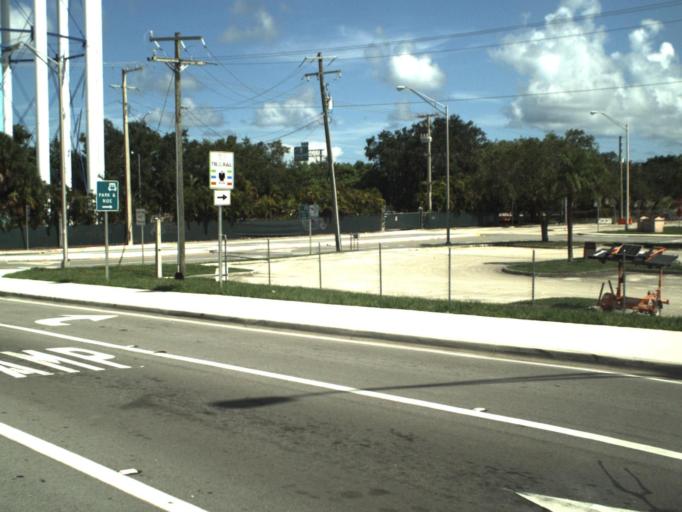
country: US
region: Florida
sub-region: Broward County
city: Hollywood
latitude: 26.0332
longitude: -80.1663
